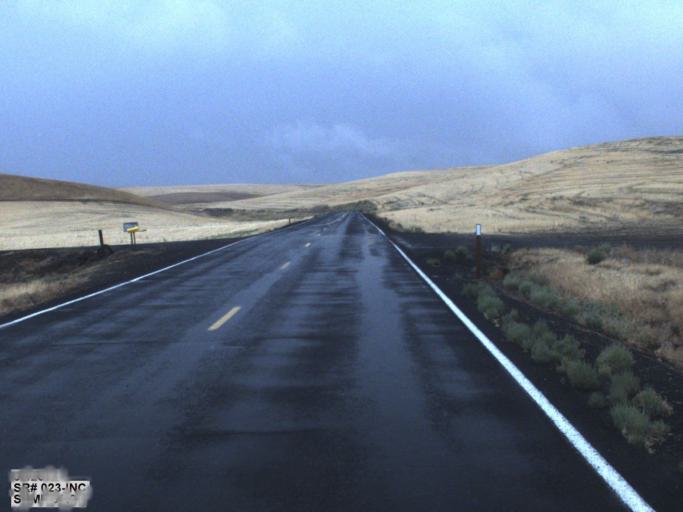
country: US
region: Washington
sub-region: Spokane County
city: Cheney
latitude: 47.1846
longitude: -117.8712
